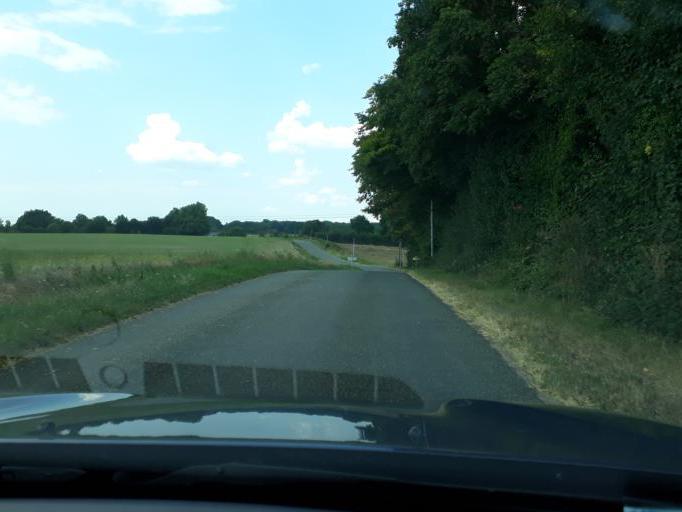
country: FR
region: Centre
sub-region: Departement du Cher
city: Jouet-sur-l'Aubois
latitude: 46.9579
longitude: 2.9460
